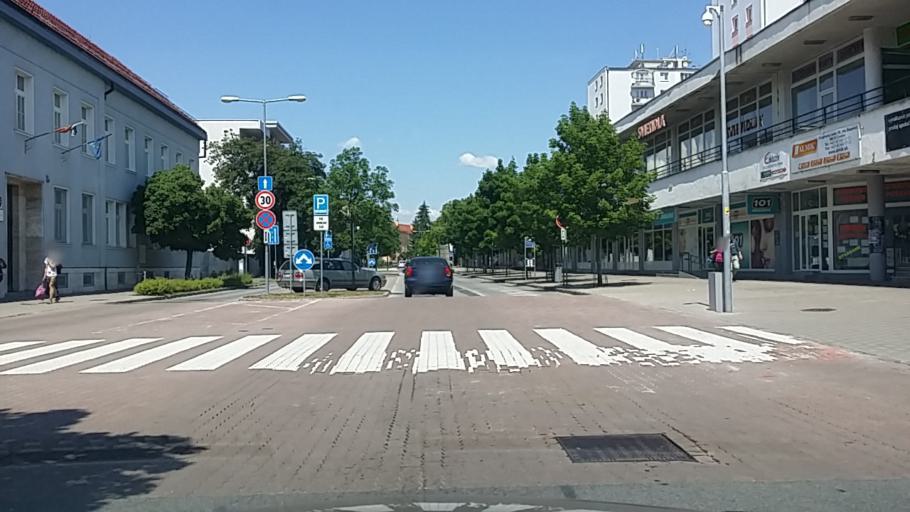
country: SK
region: Banskobystricky
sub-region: Okres Banska Bystrica
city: Zvolen
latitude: 48.5775
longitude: 19.1289
